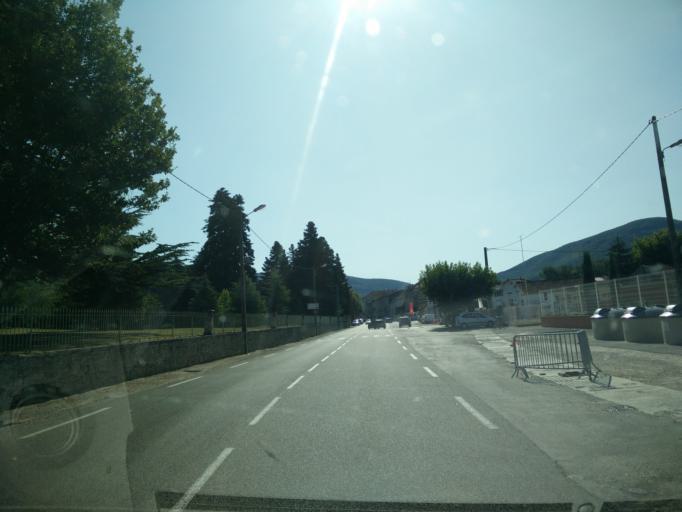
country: FR
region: Rhone-Alpes
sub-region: Departement de la Drome
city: La Begude-de-Mazenc
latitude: 44.5454
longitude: 4.9315
